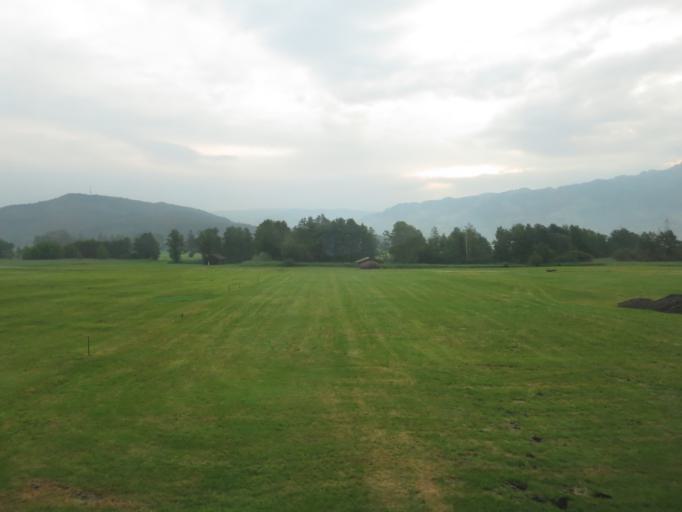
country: CH
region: Schwyz
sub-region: Bezirk March
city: Reichenburg
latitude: 47.1647
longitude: 9.0038
